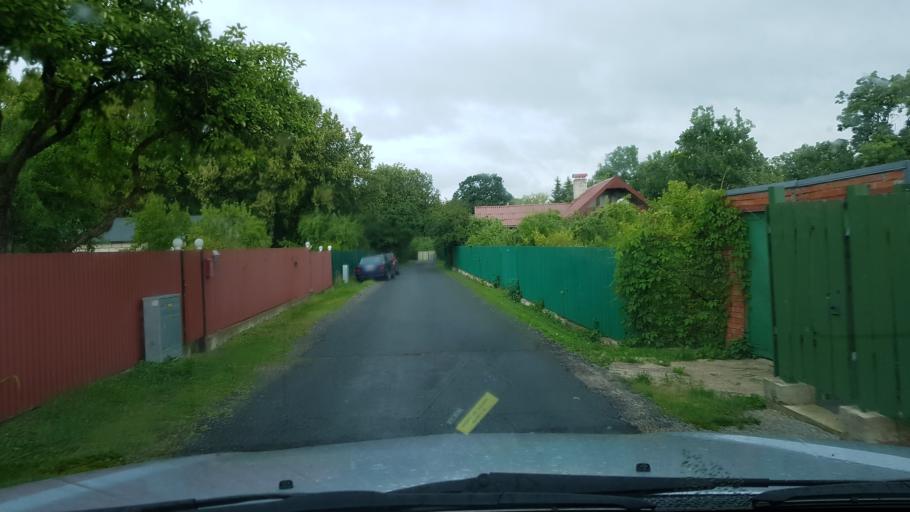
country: EE
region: Harju
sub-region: Joelaehtme vald
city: Loo
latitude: 59.4114
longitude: 24.9428
